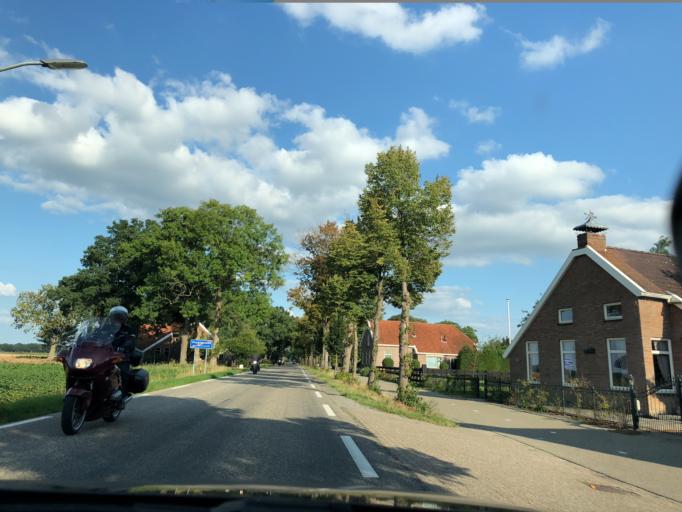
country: NL
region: Groningen
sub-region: Gemeente Vlagtwedde
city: Vlagtwedde
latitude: 53.0247
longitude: 7.1209
